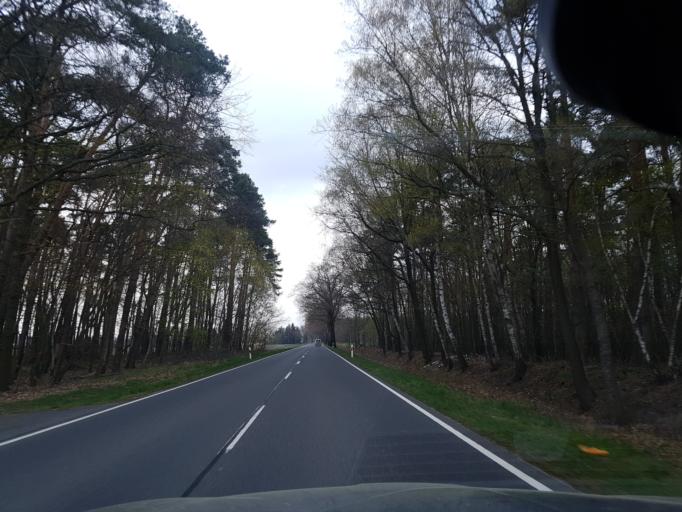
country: DE
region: Brandenburg
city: Schraden
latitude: 51.4350
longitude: 13.7061
